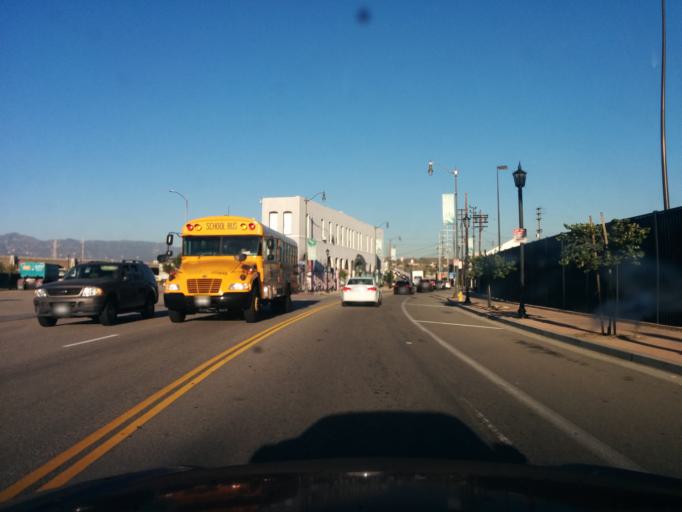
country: US
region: California
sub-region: Los Angeles County
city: Los Angeles
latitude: 34.0691
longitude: -118.2288
